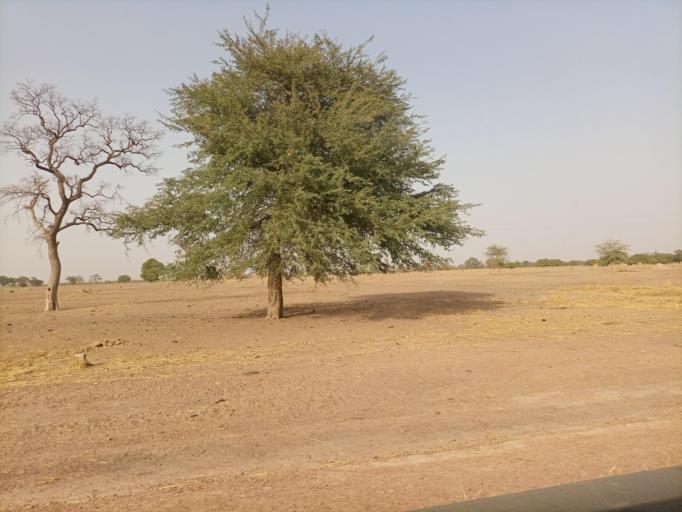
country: SN
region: Fatick
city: Passi
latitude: 14.0261
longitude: -16.3040
